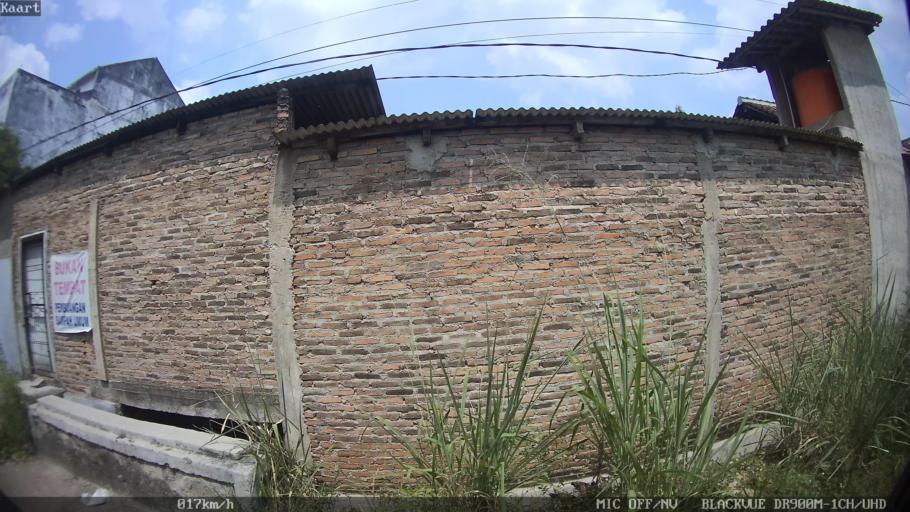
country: ID
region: Lampung
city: Pringsewu
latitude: -5.3613
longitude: 104.9816
